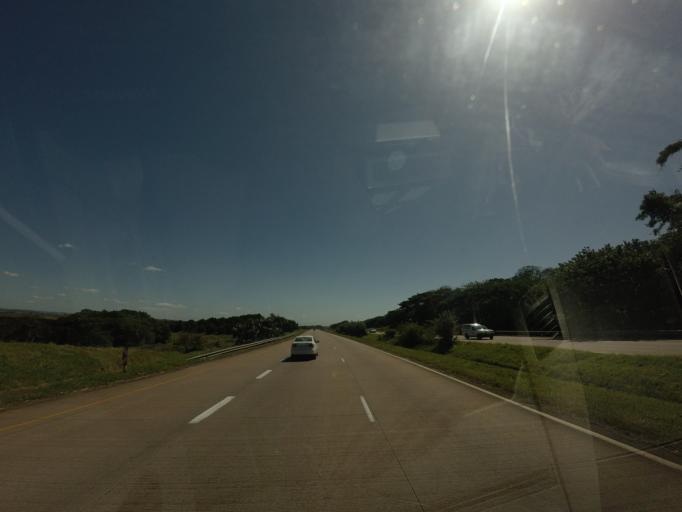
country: ZA
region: KwaZulu-Natal
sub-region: iLembe District Municipality
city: Ballitoville
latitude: -29.4770
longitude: 31.2297
